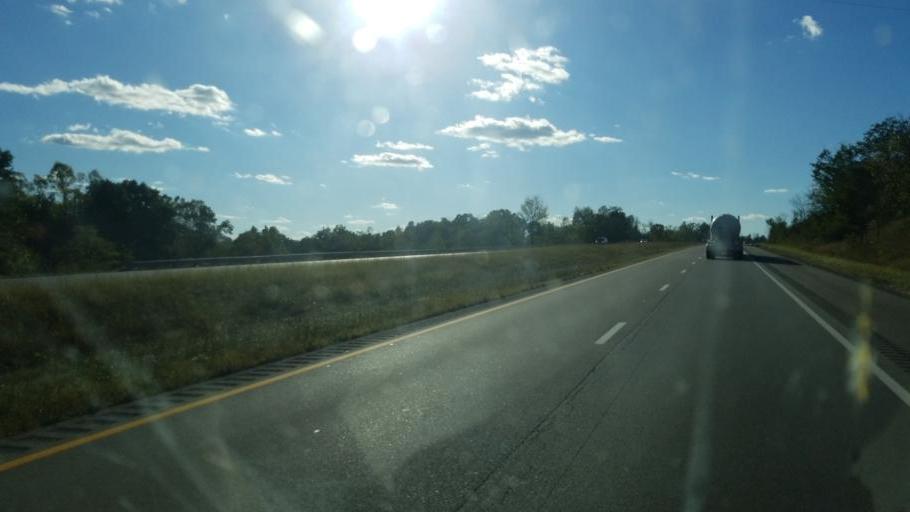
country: US
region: Ohio
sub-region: Belmont County
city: Barnesville
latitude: 40.0559
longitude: -81.2803
